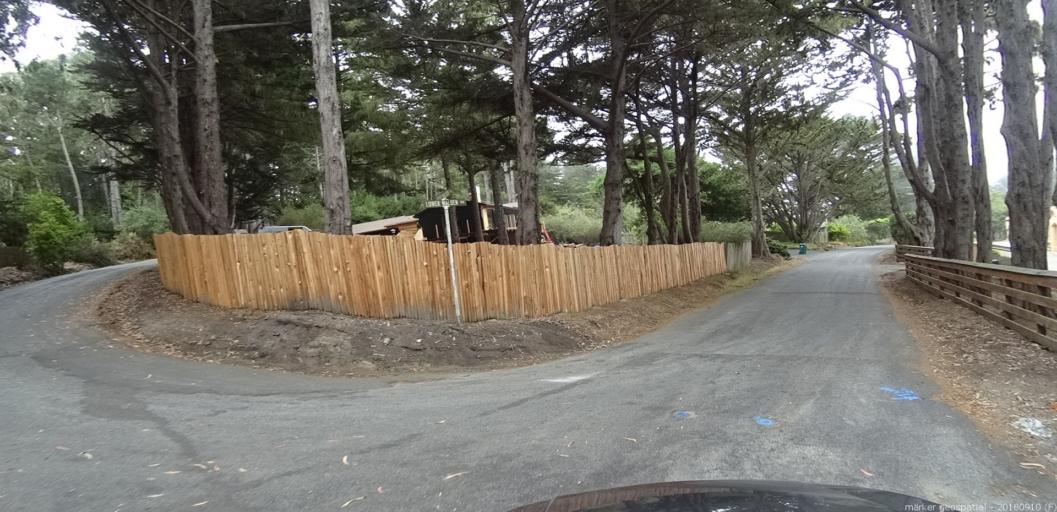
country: US
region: California
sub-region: Monterey County
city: Carmel-by-the-Sea
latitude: 36.4926
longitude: -121.9364
